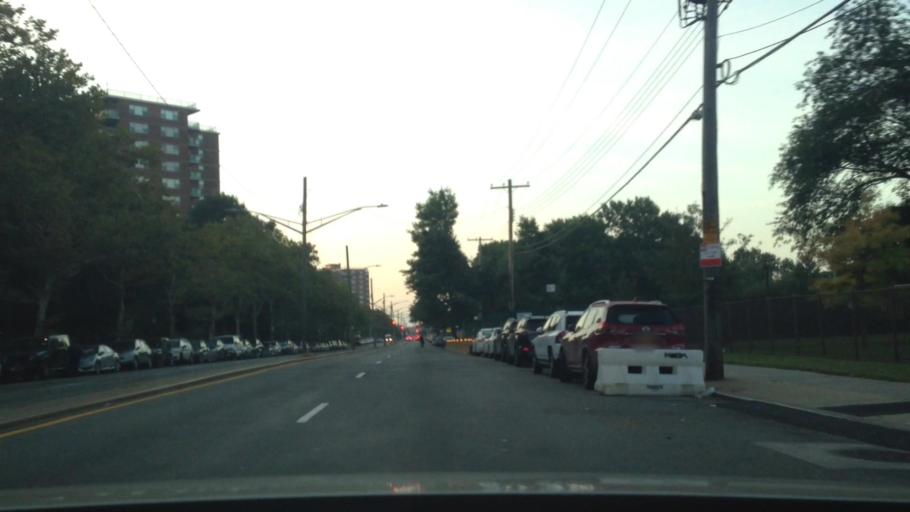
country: US
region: New York
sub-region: Queens County
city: Jamaica
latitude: 40.6761
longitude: -73.7779
